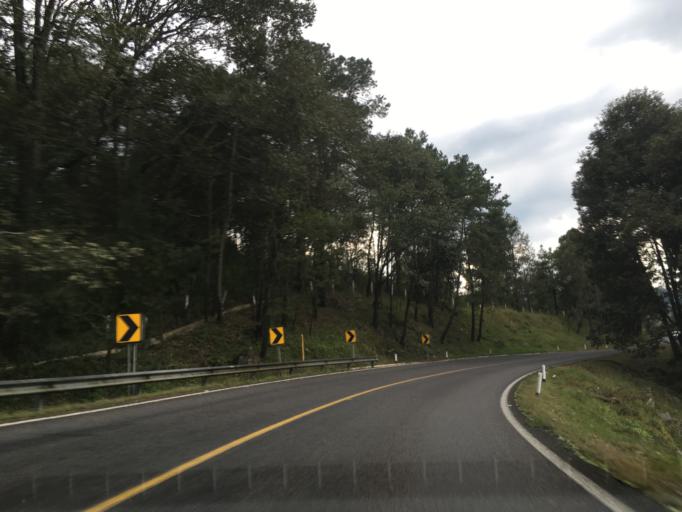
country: MX
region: Michoacan
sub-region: Patzcuaro
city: Santa Maria Huiramangaro (San Juan Tumbio)
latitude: 19.4879
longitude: -101.7238
